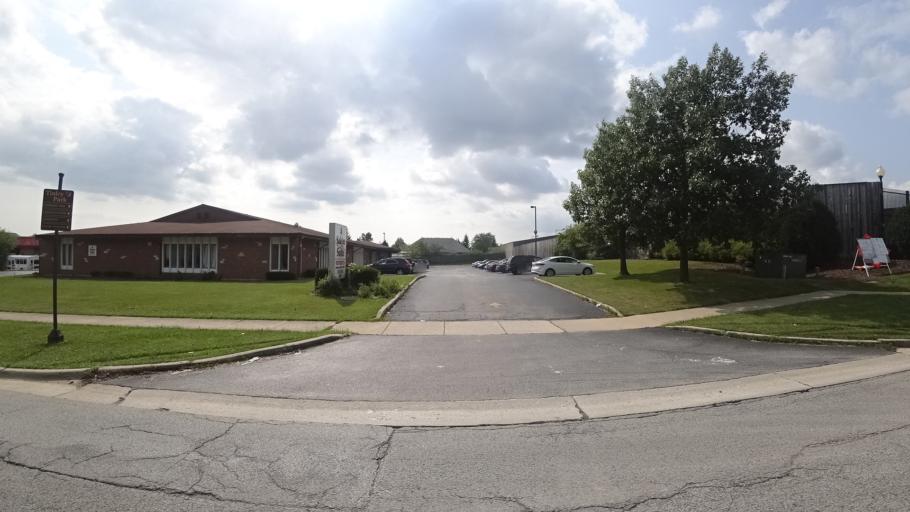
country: US
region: Illinois
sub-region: Cook County
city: Tinley Park
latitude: 41.5992
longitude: -87.7852
